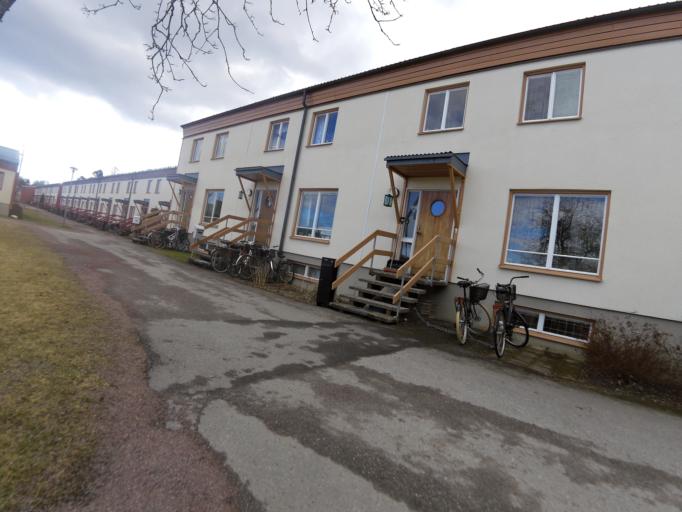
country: SE
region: Gaevleborg
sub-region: Gavle Kommun
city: Gavle
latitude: 60.6863
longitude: 17.1088
